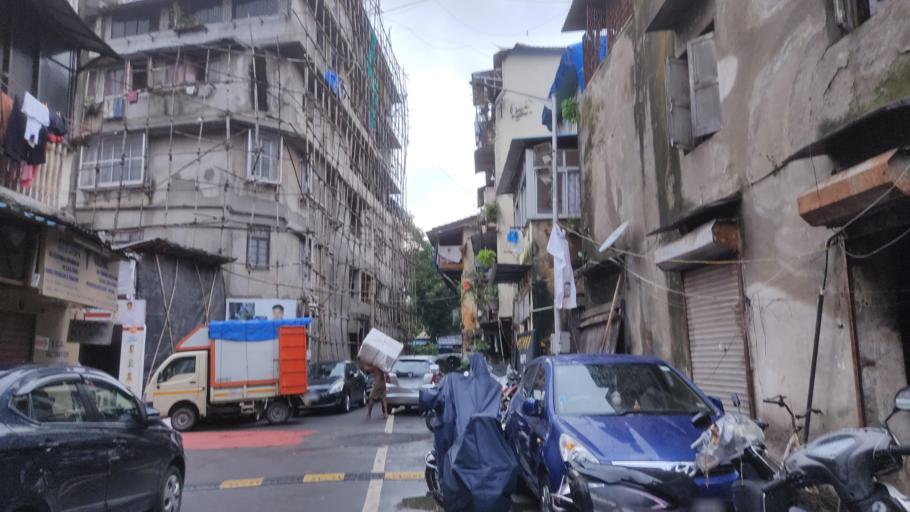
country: IN
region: Maharashtra
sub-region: Raigarh
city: Uran
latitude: 18.9483
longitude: 72.8253
